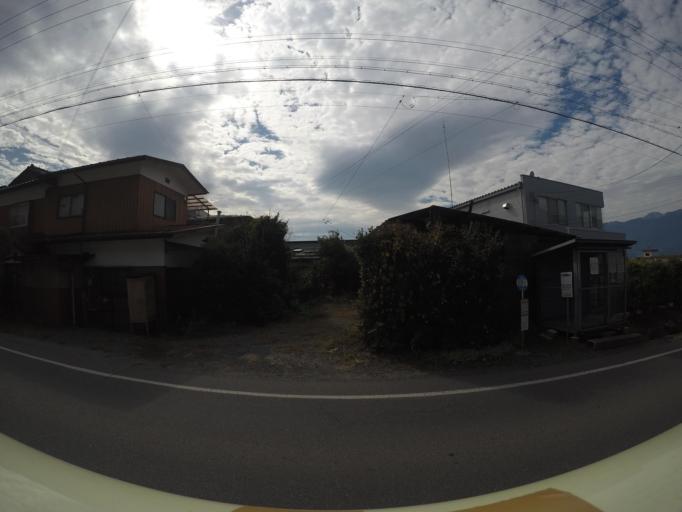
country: JP
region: Nagano
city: Ina
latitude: 35.8376
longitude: 137.9859
